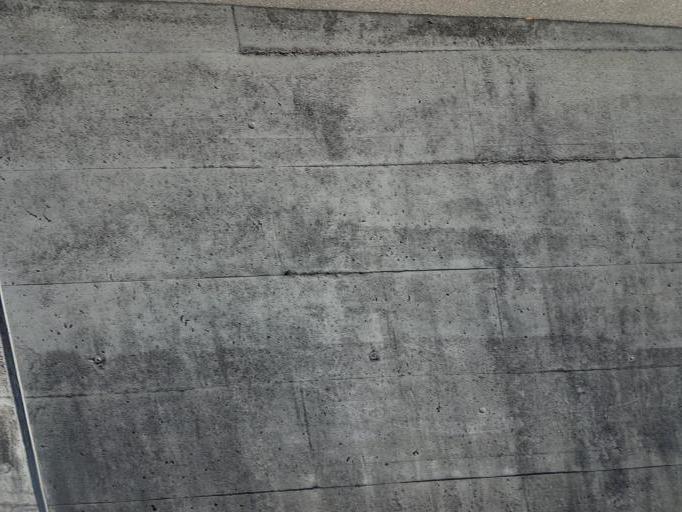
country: CH
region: Schwyz
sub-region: Bezirk Kuessnacht
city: Kussnacht
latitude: 47.0867
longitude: 8.4325
